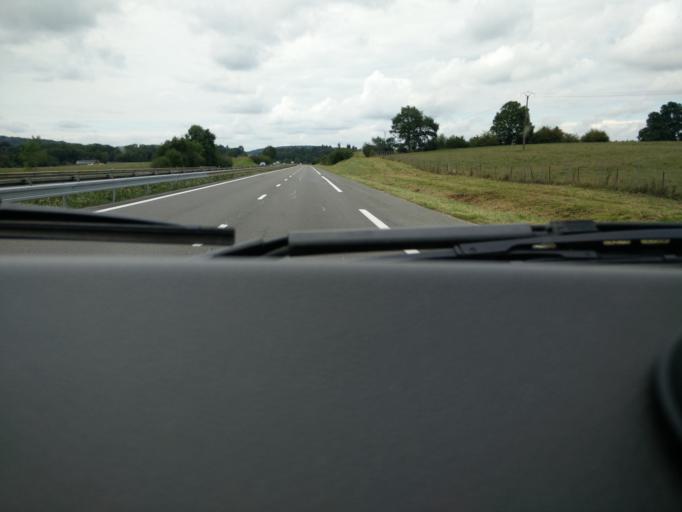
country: FR
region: Champagne-Ardenne
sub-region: Departement des Ardennes
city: Vrigne-aux-Bois
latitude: 49.7210
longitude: 4.8619
